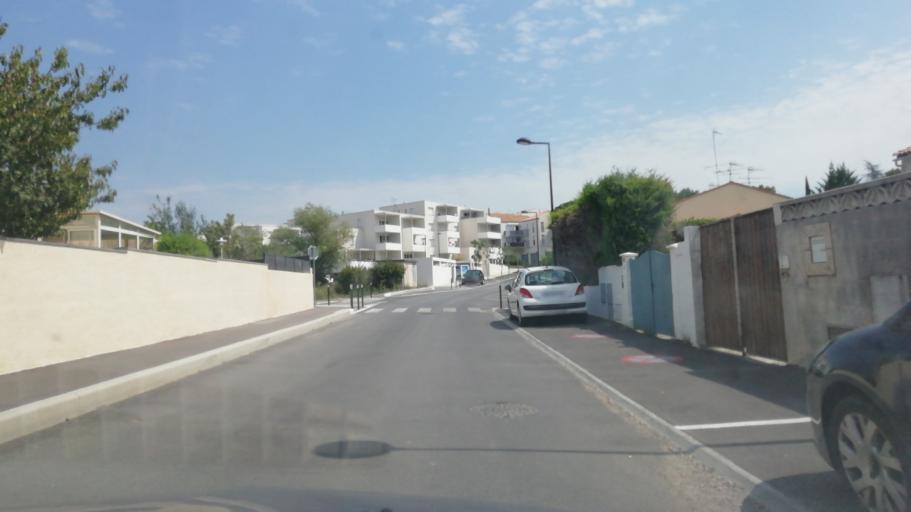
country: FR
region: Languedoc-Roussillon
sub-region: Departement de l'Herault
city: Saint-Mathieu-de-Treviers
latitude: 43.7680
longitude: 3.8611
